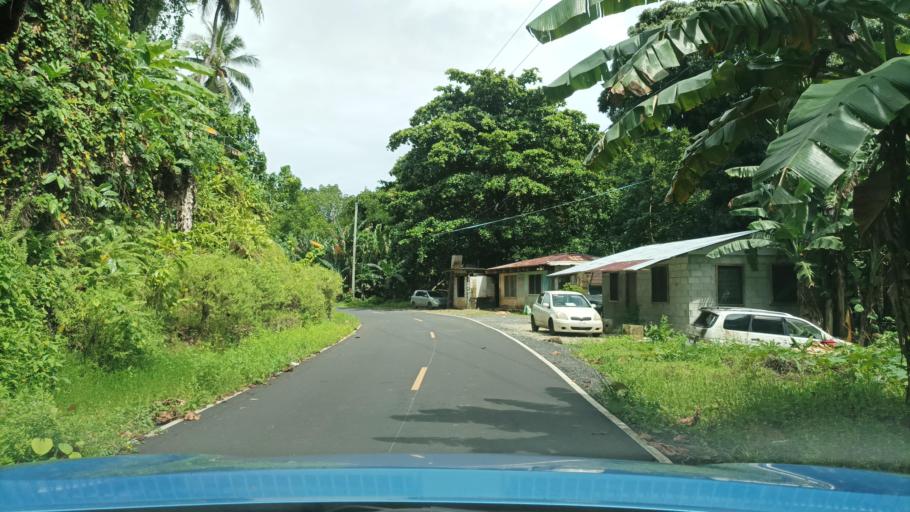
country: FM
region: Pohnpei
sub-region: Madolenihm Municipality
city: Madolenihm Municipality Government
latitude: 6.8764
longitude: 158.3337
